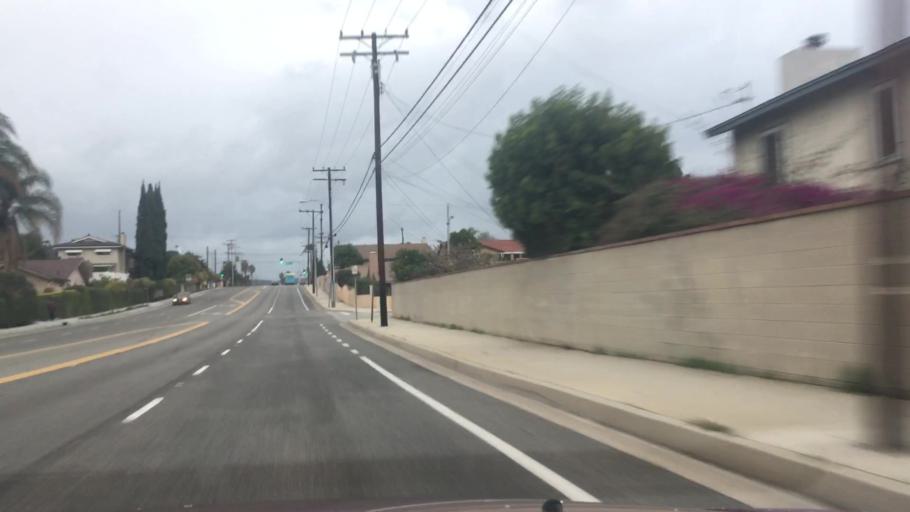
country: US
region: California
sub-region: Los Angeles County
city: East La Mirada
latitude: 33.9225
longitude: -117.9944
